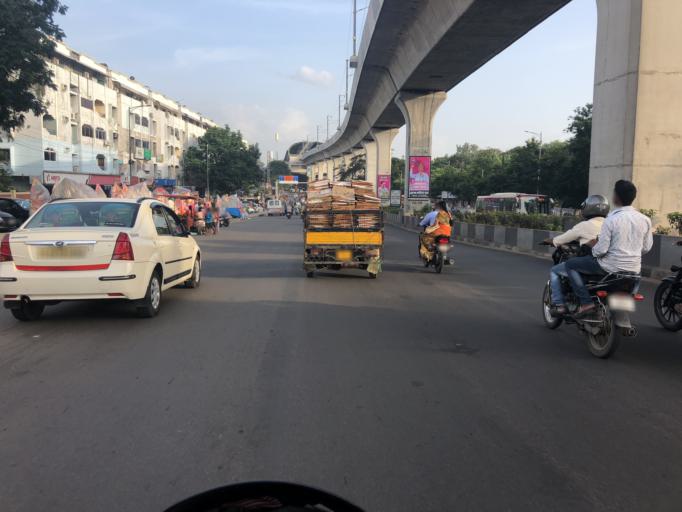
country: IN
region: Telangana
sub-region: Rangareddi
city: Kukatpalli
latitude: 17.4501
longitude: 78.4370
